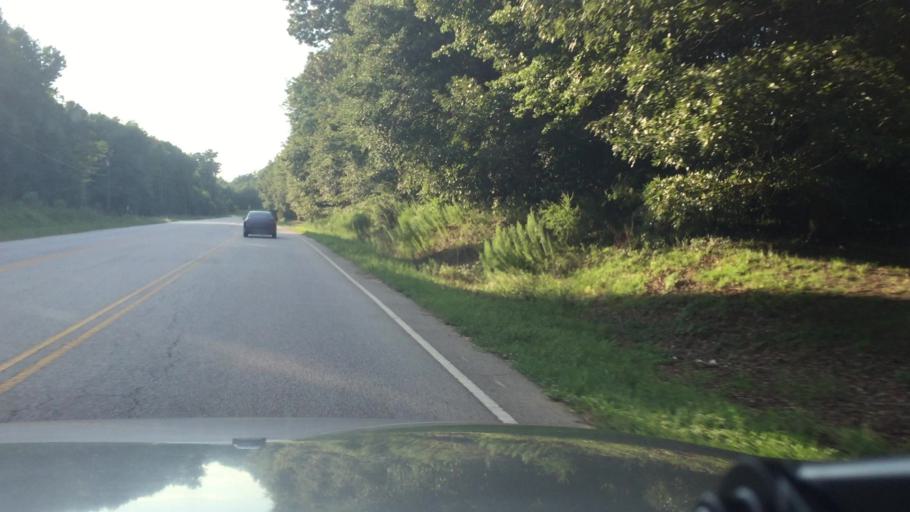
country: US
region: South Carolina
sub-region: Sumter County
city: Lakewood
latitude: 33.8715
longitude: -80.3637
